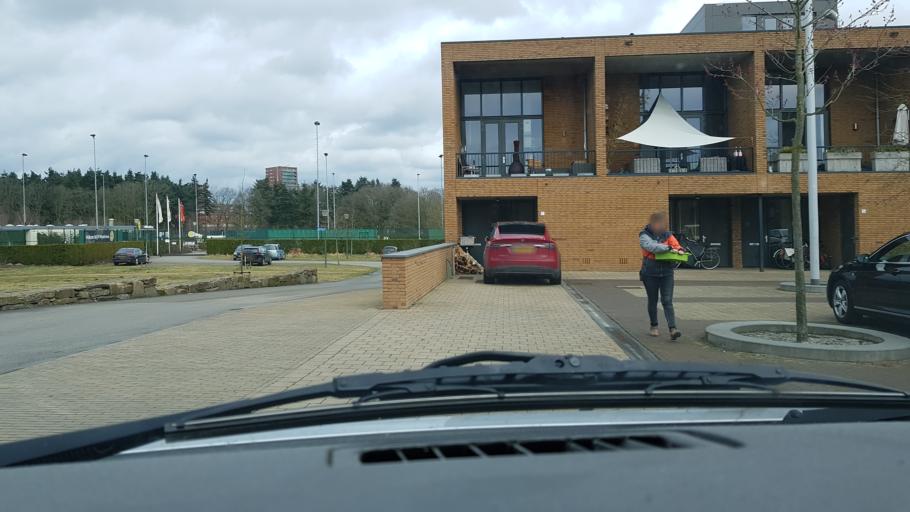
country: NL
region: North Brabant
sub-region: Gemeente Eindhoven
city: Meerhoven
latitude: 51.4377
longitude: 5.4043
